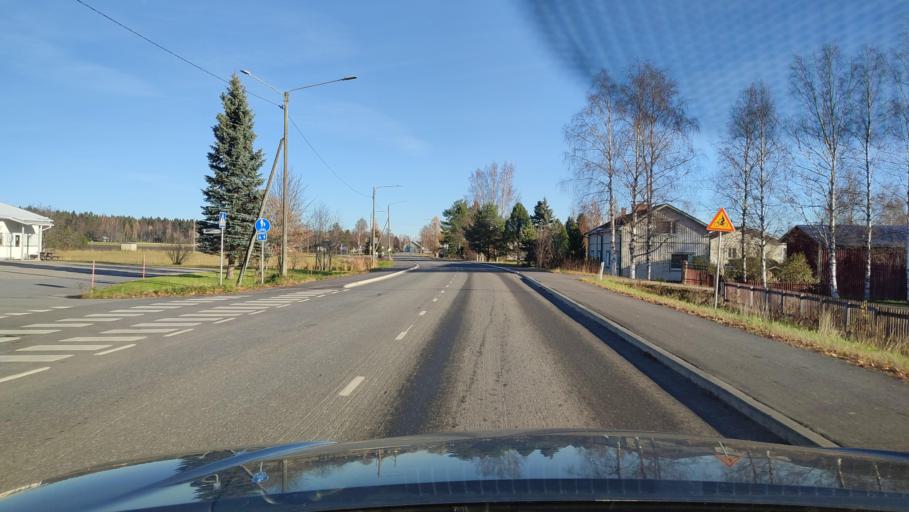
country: FI
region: Southern Ostrobothnia
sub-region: Suupohja
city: Karijoki
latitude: 62.3084
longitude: 21.7084
